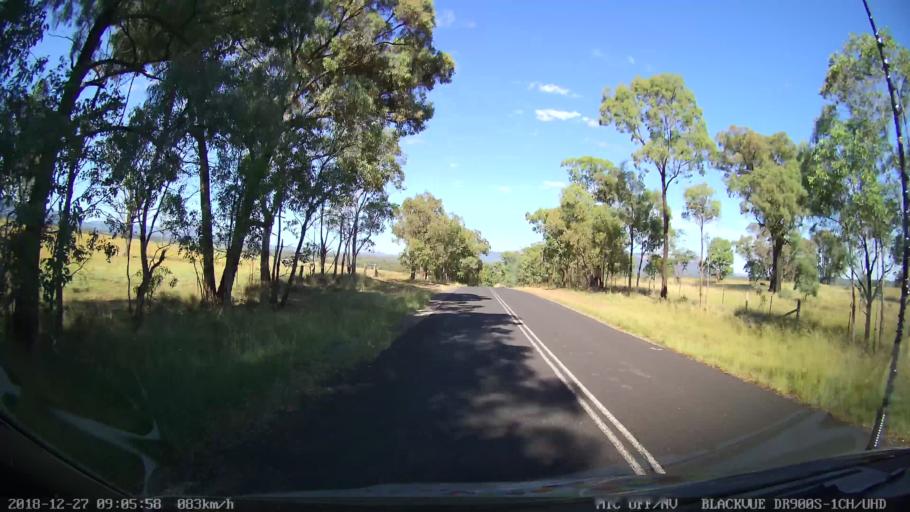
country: AU
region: New South Wales
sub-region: Lithgow
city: Portland
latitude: -33.1198
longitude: 150.1734
